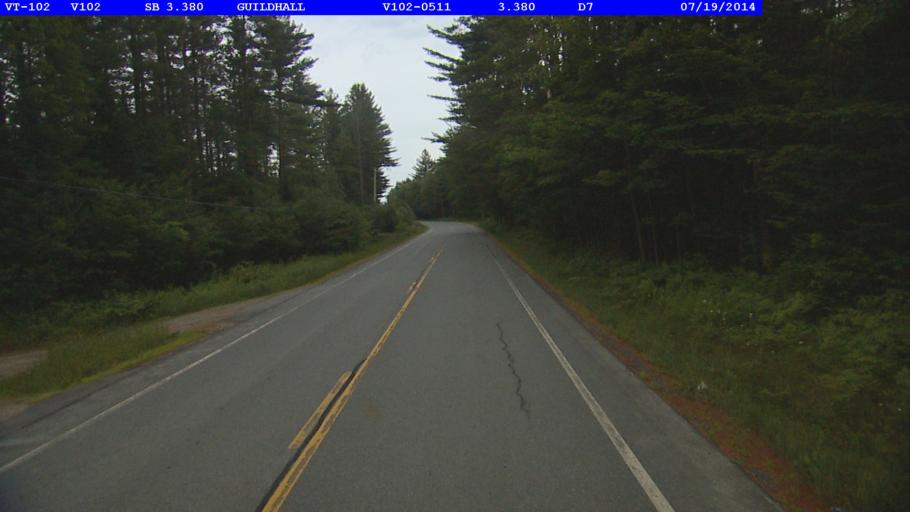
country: US
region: New Hampshire
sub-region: Coos County
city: Northumberland
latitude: 44.5417
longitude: -71.5836
